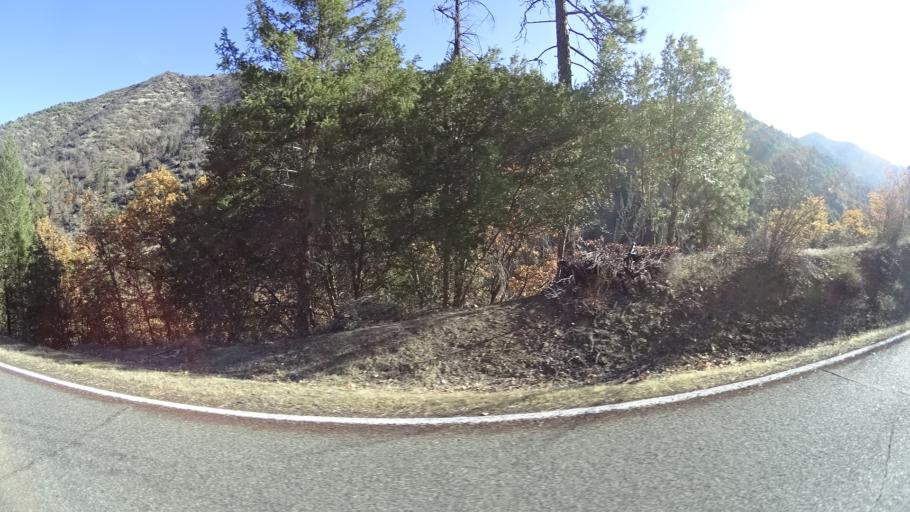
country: US
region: California
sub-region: Siskiyou County
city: Yreka
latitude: 41.9051
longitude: -122.8300
